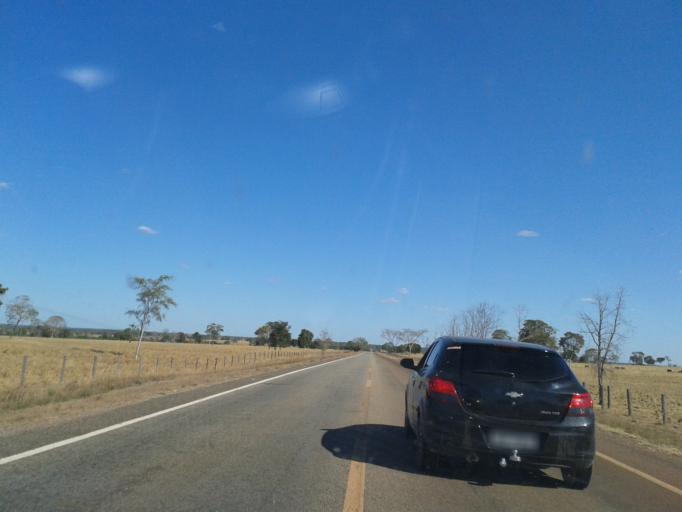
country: BR
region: Goias
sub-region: Crixas
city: Crixas
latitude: -14.2550
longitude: -50.3974
